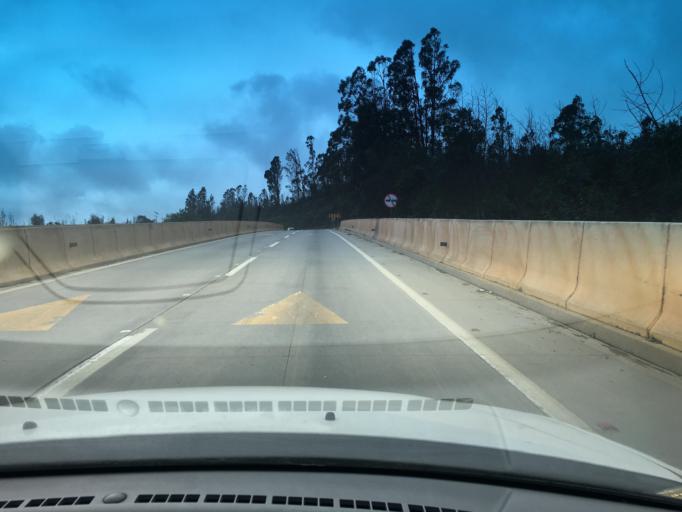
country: CL
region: Valparaiso
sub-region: Provincia de Valparaiso
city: Valparaiso
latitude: -33.0905
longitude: -71.6110
